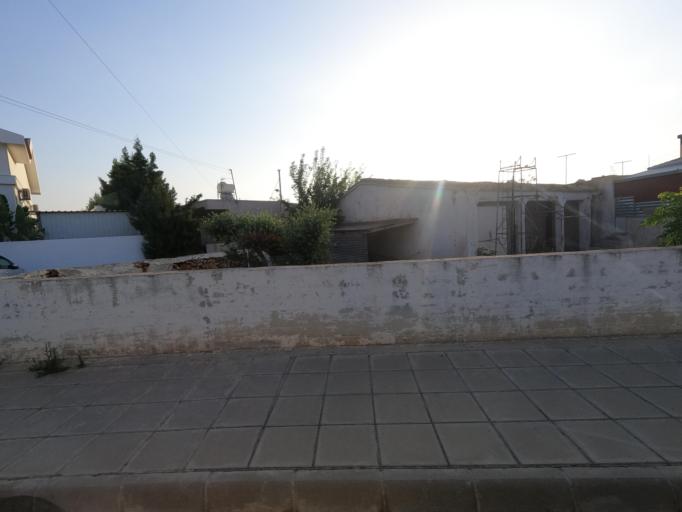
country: CY
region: Ammochostos
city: Paralimni
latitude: 35.0272
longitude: 33.9580
